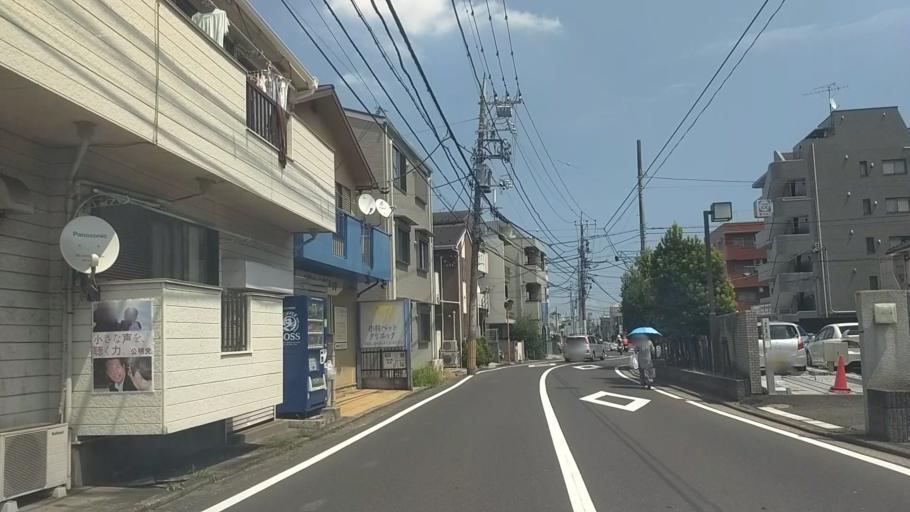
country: JP
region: Kanagawa
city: Yokohama
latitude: 35.4869
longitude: 139.6164
